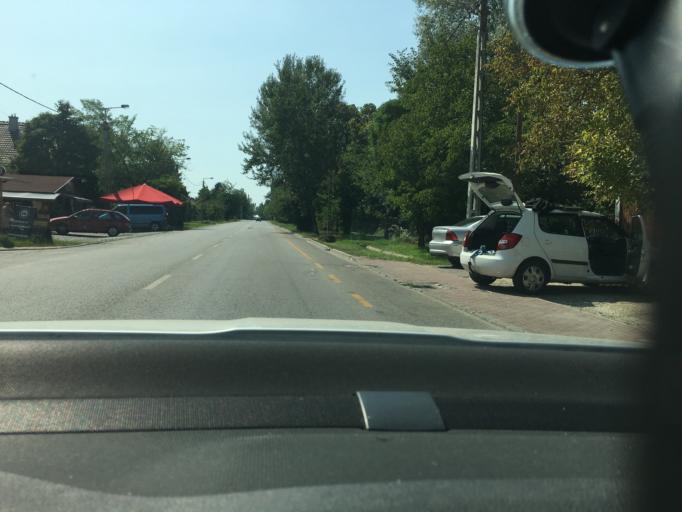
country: HU
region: Budapest
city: Budapest XVI. keruelet
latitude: 47.5099
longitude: 19.2117
